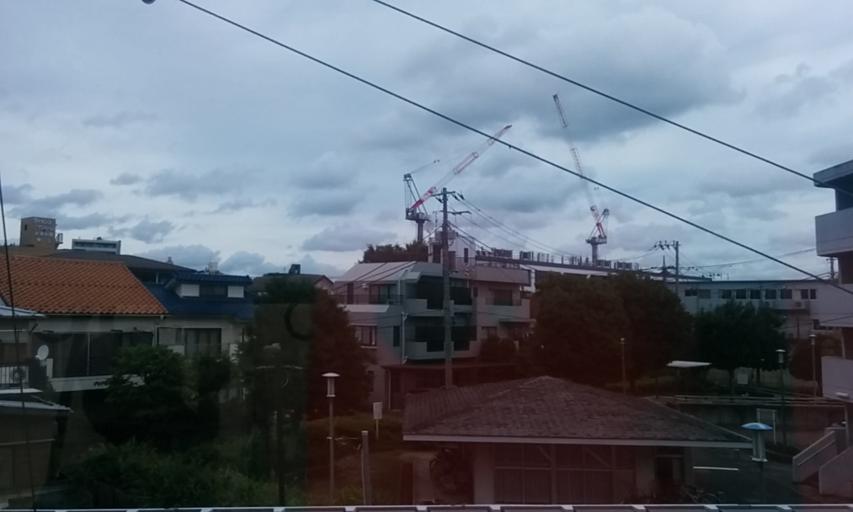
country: JP
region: Tokyo
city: Musashino
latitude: 35.7479
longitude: 139.5899
